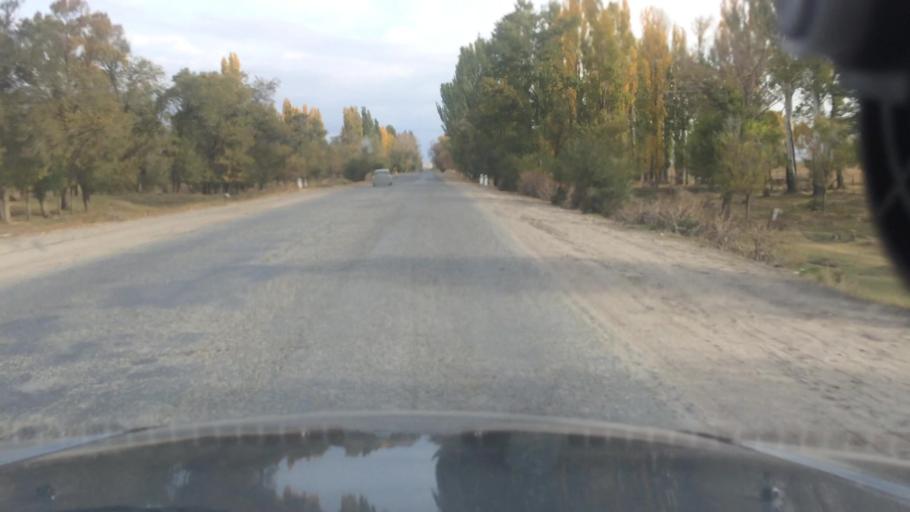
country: KG
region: Ysyk-Koel
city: Karakol
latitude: 42.5401
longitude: 78.3841
